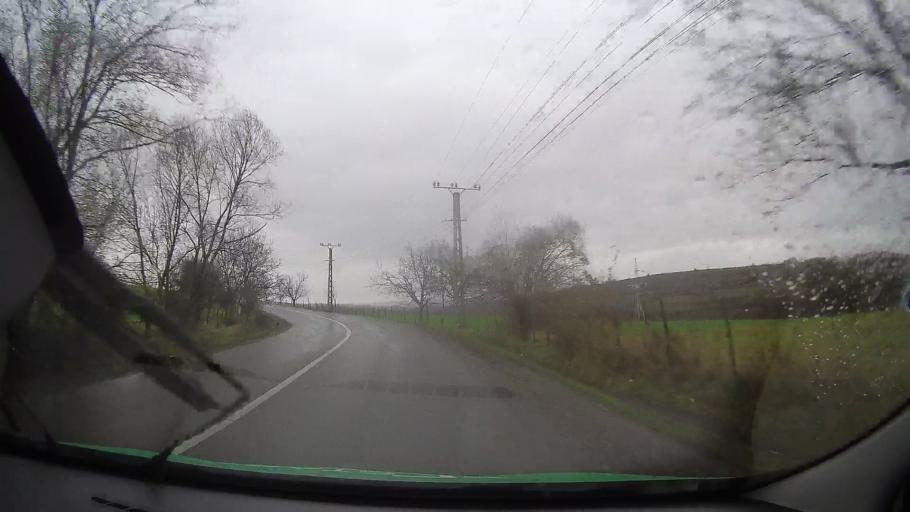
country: RO
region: Mures
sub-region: Comuna Brancovenesti
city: Valenii de Mures
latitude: 46.9215
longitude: 24.7752
